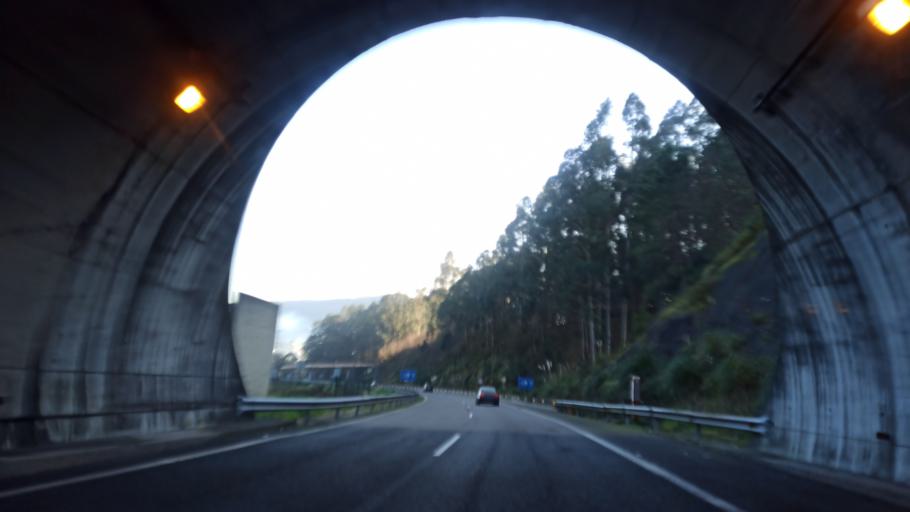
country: ES
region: Galicia
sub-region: Provincia da Coruna
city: Mino
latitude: 43.3947
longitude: -8.1682
